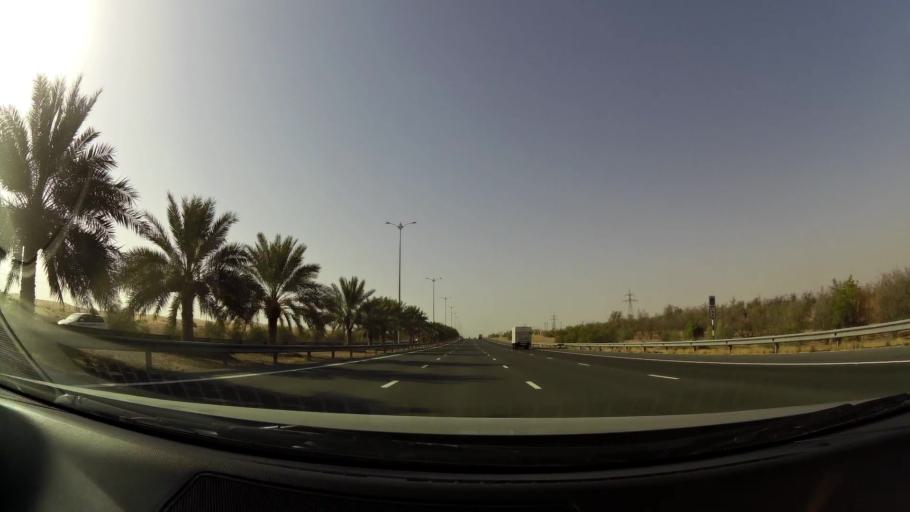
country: OM
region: Al Buraimi
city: Al Buraymi
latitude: 24.6233
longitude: 55.7242
